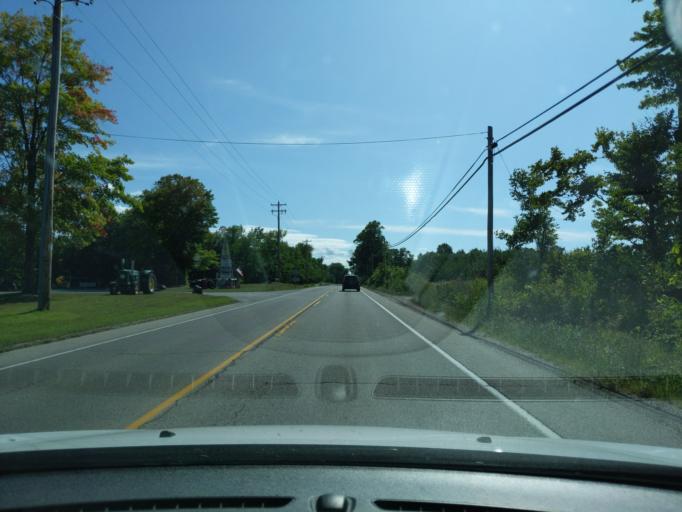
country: US
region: Wisconsin
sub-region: Door County
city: Sturgeon Bay
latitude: 45.2272
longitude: -87.1022
